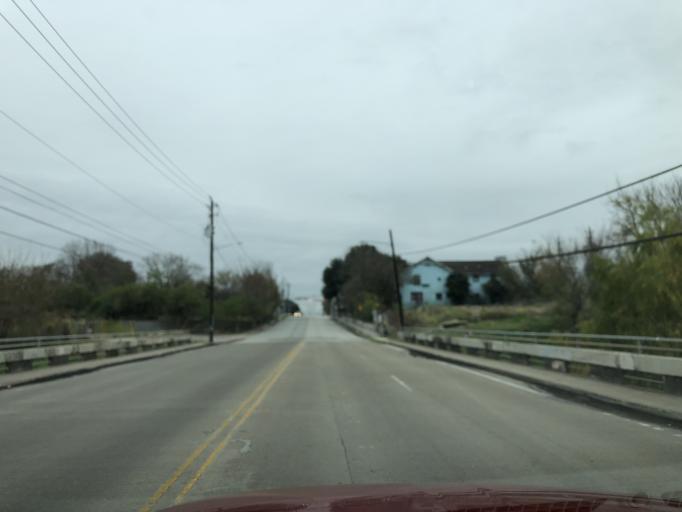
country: US
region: Texas
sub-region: Harris County
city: Houston
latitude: 29.7852
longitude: -95.3660
